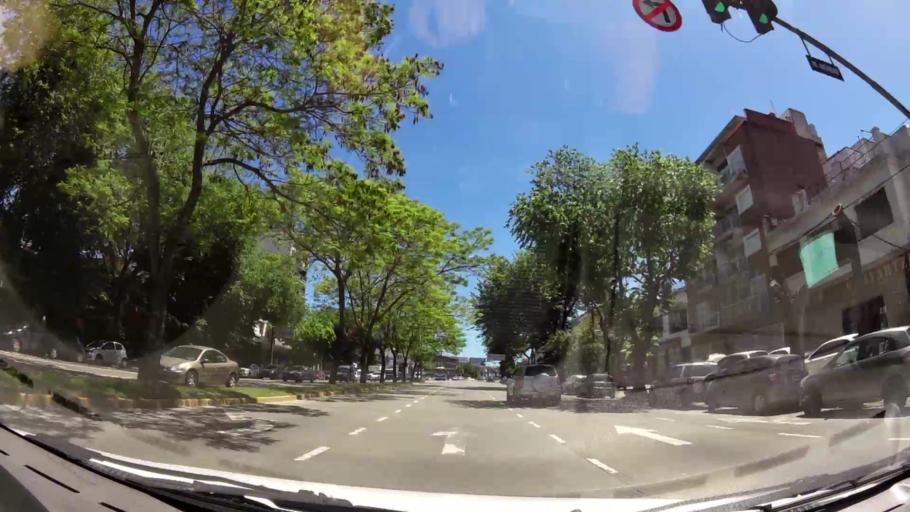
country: AR
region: Buenos Aires
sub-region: Partido de Vicente Lopez
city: Olivos
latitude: -34.4987
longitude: -58.4971
